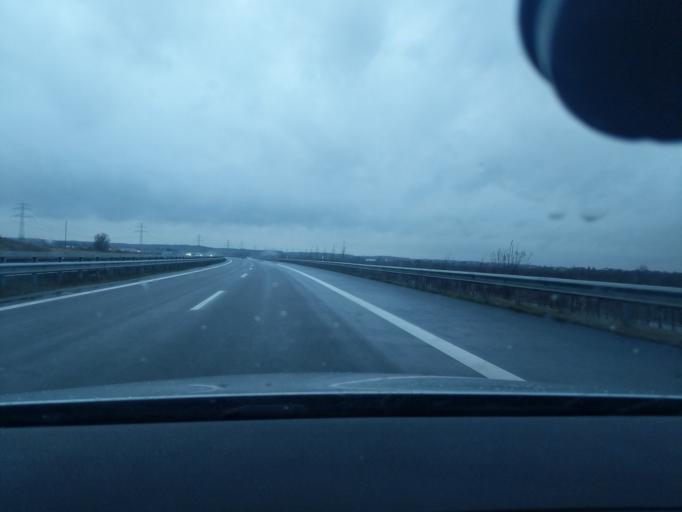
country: DE
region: Lower Saxony
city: Neuenkirchen
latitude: 53.5114
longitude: 9.6254
